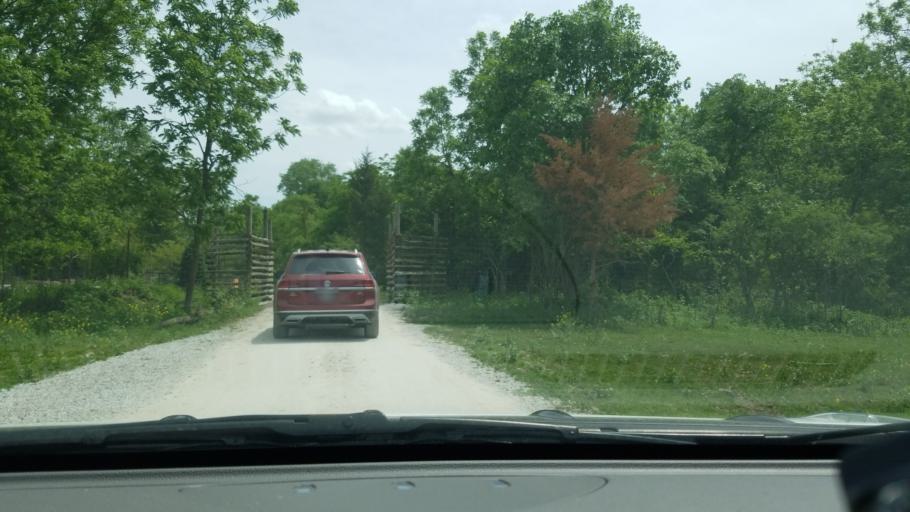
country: US
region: Nebraska
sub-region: Saunders County
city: Ashland
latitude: 41.0156
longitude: -96.2952
